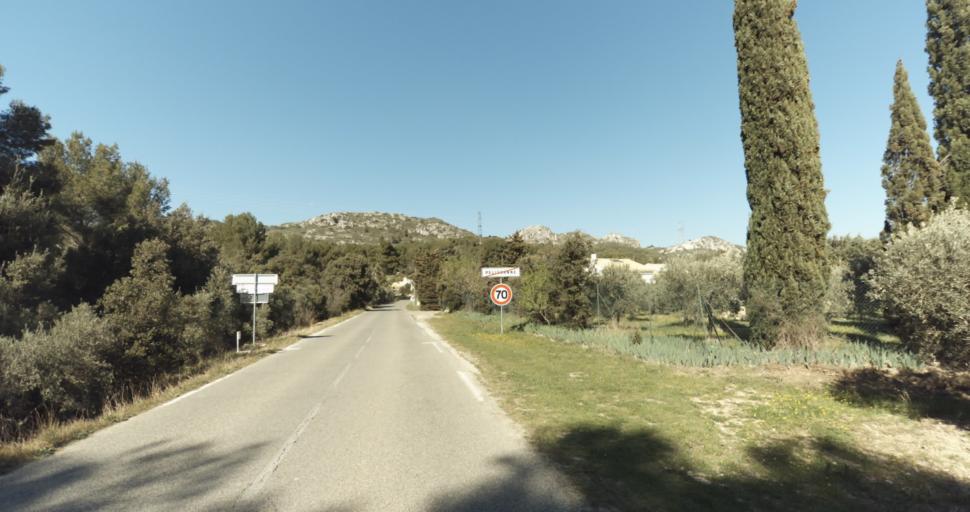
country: FR
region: Provence-Alpes-Cote d'Azur
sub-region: Departement des Bouches-du-Rhone
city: Pelissanne
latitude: 43.6465
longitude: 5.1557
